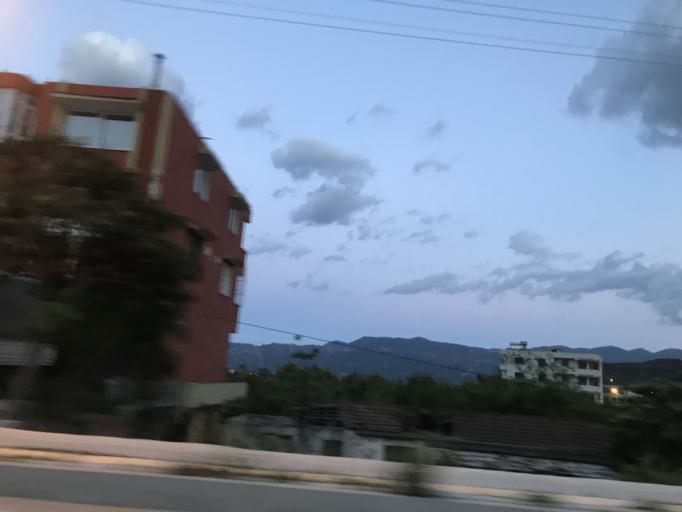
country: TR
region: Hatay
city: Uzunbag
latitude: 36.1345
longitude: 36.0413
